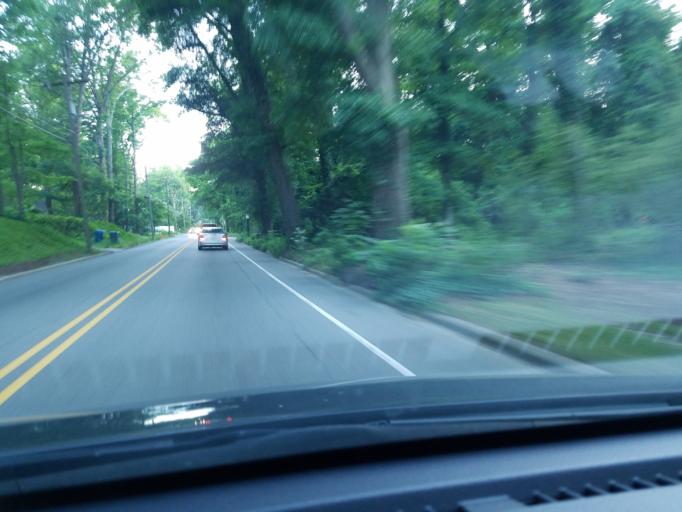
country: US
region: North Carolina
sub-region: Durham County
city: Durham
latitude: 35.9788
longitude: -78.9156
